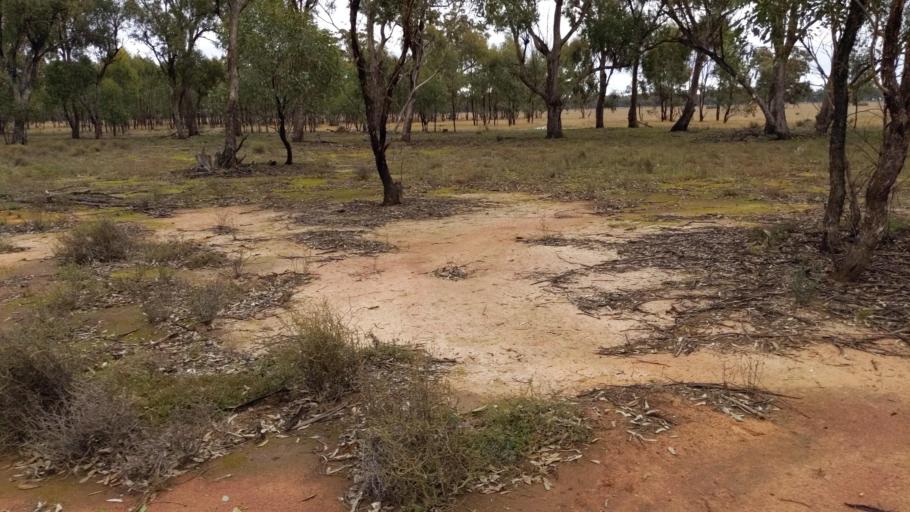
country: AU
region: New South Wales
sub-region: Coolamon
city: Coolamon
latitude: -34.8630
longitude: 146.9199
